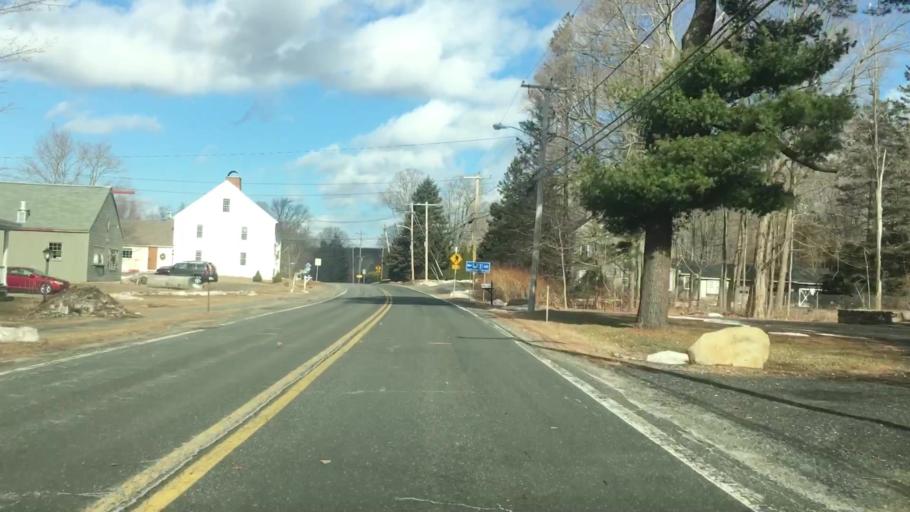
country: US
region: Massachusetts
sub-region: Hampden County
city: Wales
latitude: 42.0667
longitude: -72.2224
